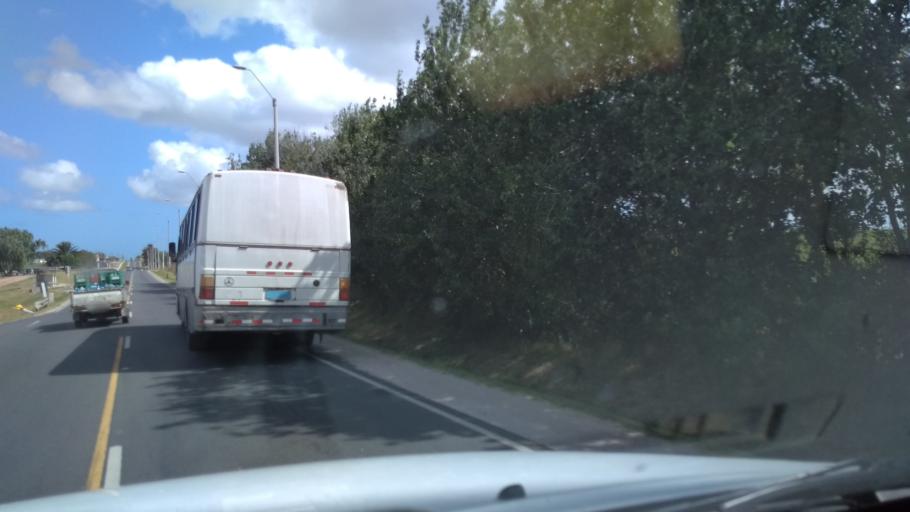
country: UY
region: Canelones
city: Joaquin Suarez
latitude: -34.7544
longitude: -56.0193
